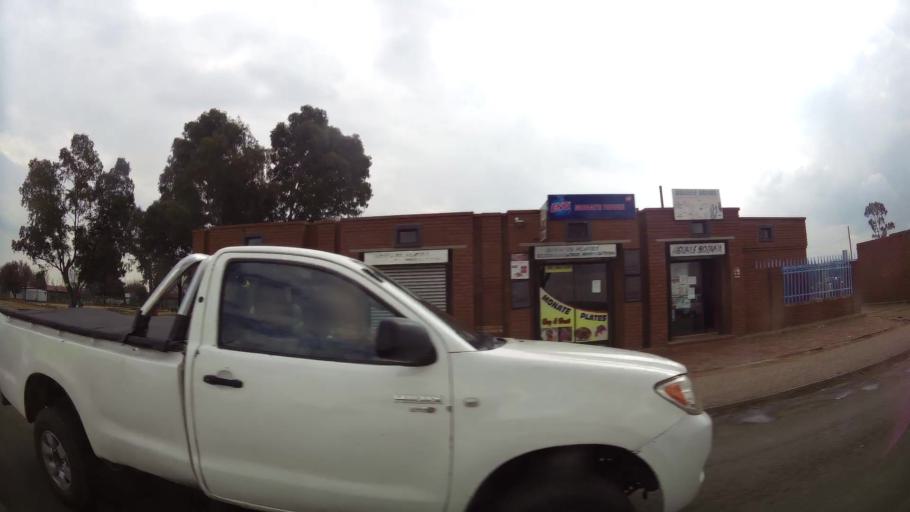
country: ZA
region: Gauteng
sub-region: Ekurhuleni Metropolitan Municipality
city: Germiston
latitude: -26.3878
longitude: 28.1618
